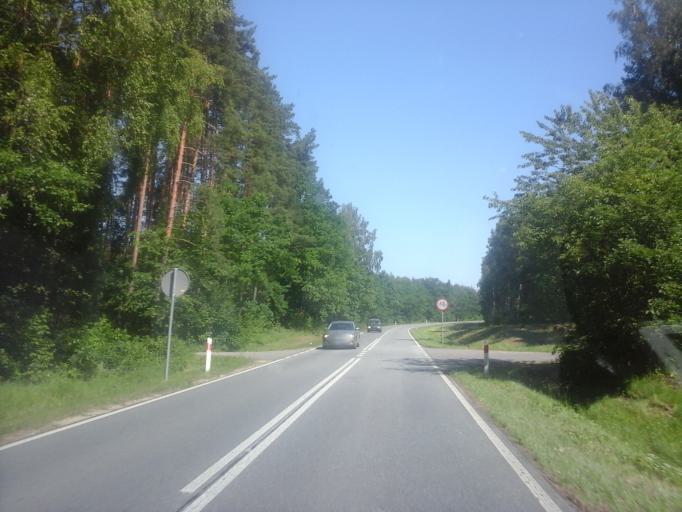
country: PL
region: West Pomeranian Voivodeship
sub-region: Koszalin
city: Koszalin
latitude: 54.0853
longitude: 16.1601
